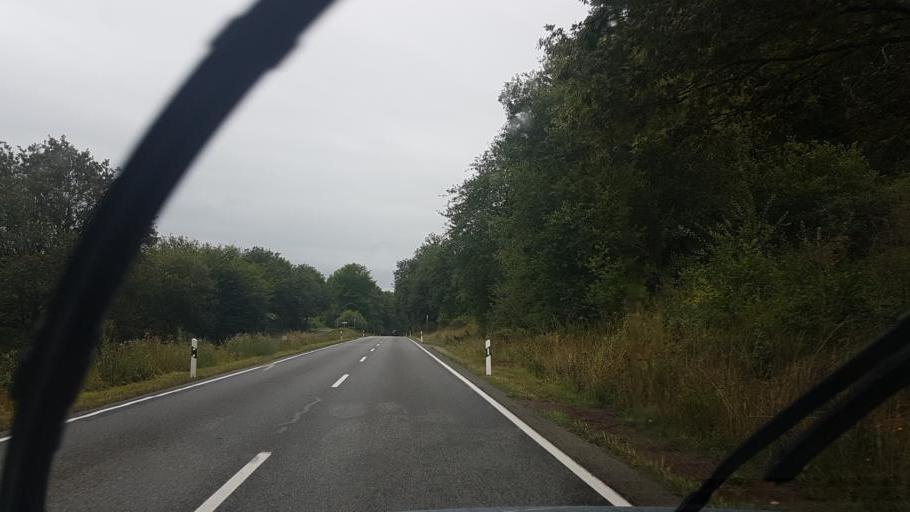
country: DE
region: Saarland
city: Nonnweiler
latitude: 49.5734
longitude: 6.9562
